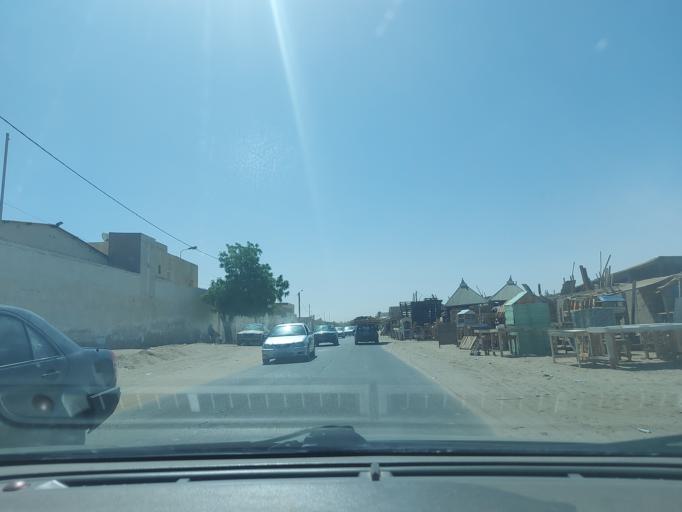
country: MR
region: Nouakchott
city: Nouakchott
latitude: 18.0624
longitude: -15.9779
